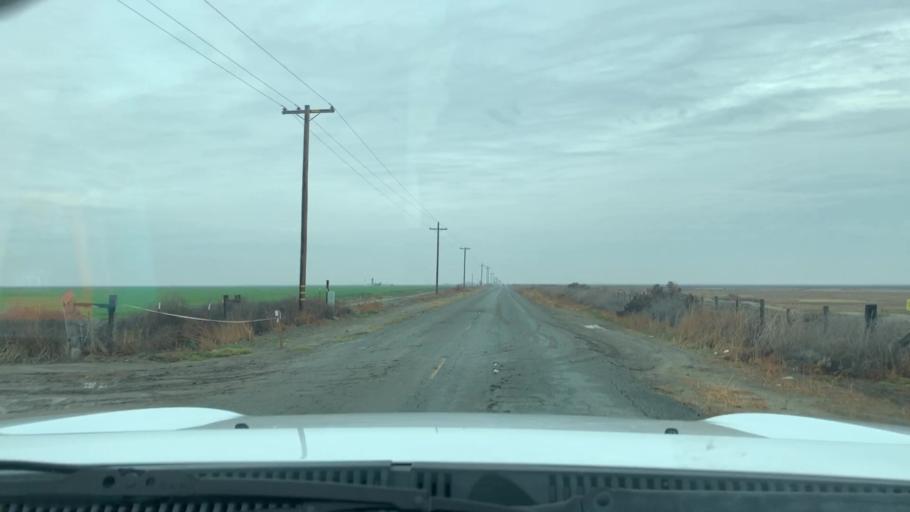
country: US
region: California
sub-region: Tulare County
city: Alpaugh
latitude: 35.7609
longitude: -119.5351
